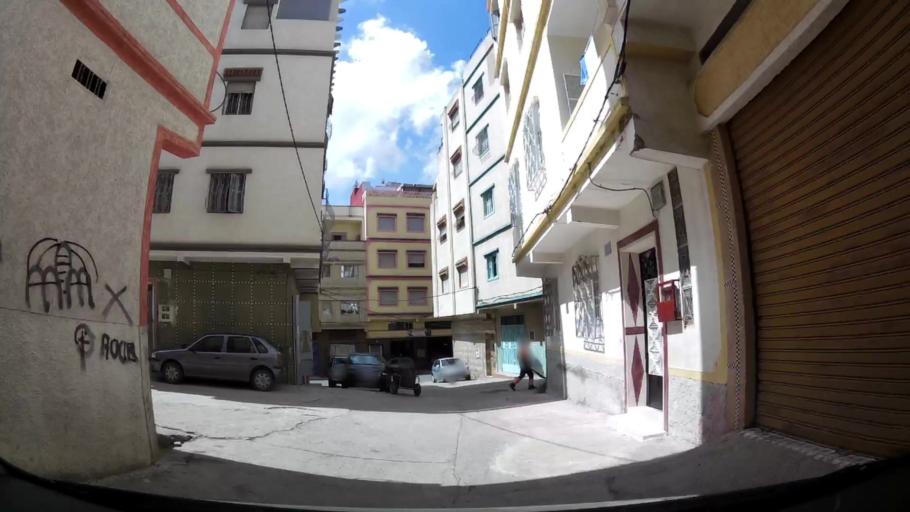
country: MA
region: Tanger-Tetouan
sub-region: Tanger-Assilah
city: Tangier
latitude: 35.7552
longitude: -5.8172
